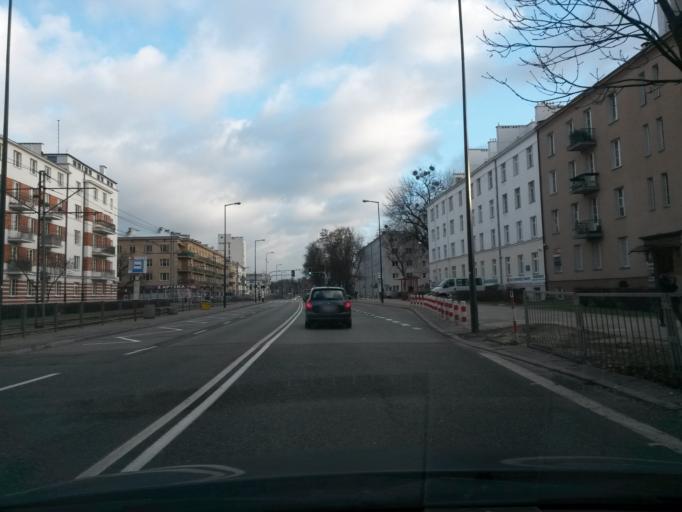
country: PL
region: Masovian Voivodeship
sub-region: Warszawa
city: Zoliborz
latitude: 52.2707
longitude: 20.9781
